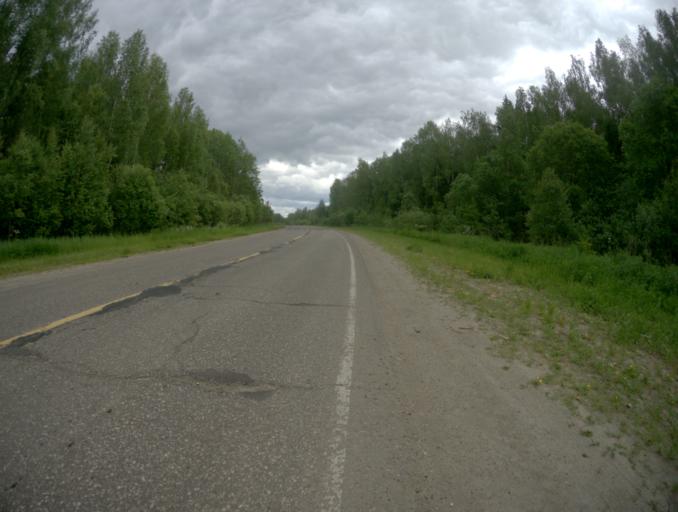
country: RU
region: Ivanovo
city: Kolobovo
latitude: 56.6236
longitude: 41.3335
